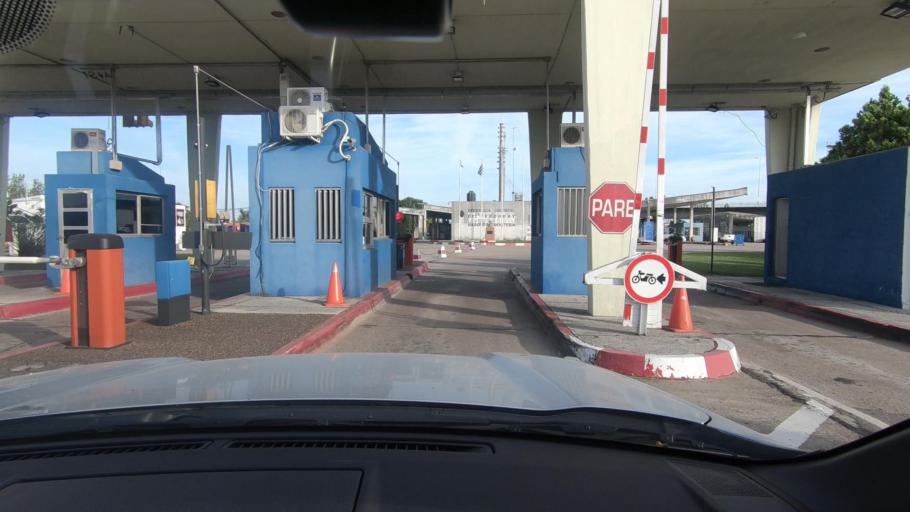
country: AR
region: Entre Rios
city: Colon
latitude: -32.2508
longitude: -58.1427
